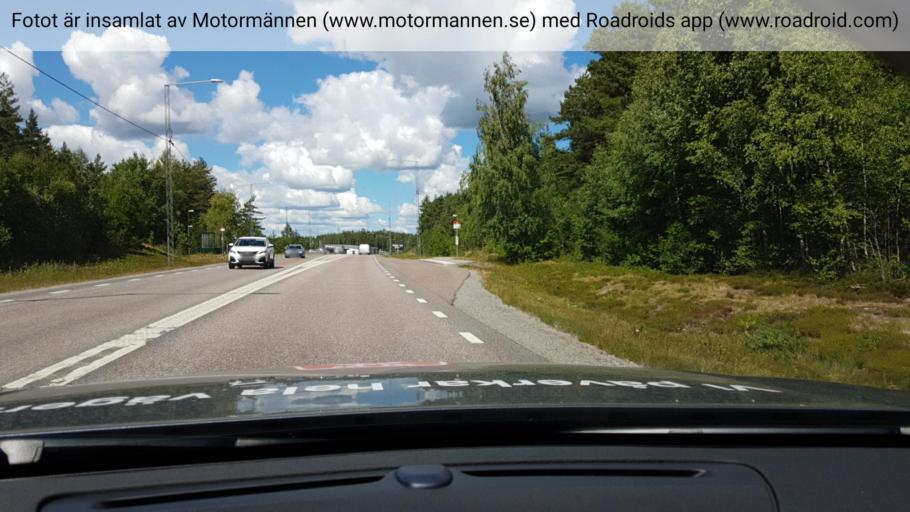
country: SE
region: Stockholm
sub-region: Vallentuna Kommun
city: Vallentuna
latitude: 59.5117
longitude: 18.0960
